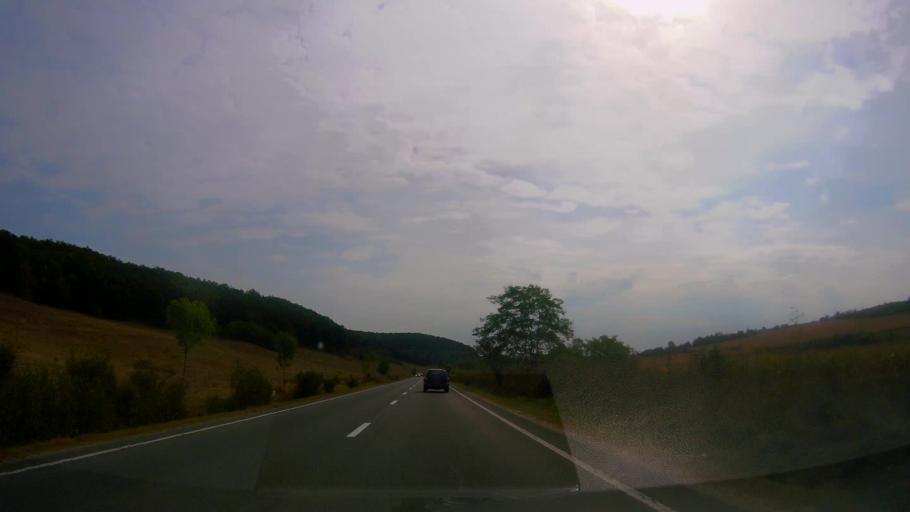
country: RO
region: Salaj
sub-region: Comuna Hida
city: Hida
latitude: 47.0553
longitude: 23.2286
